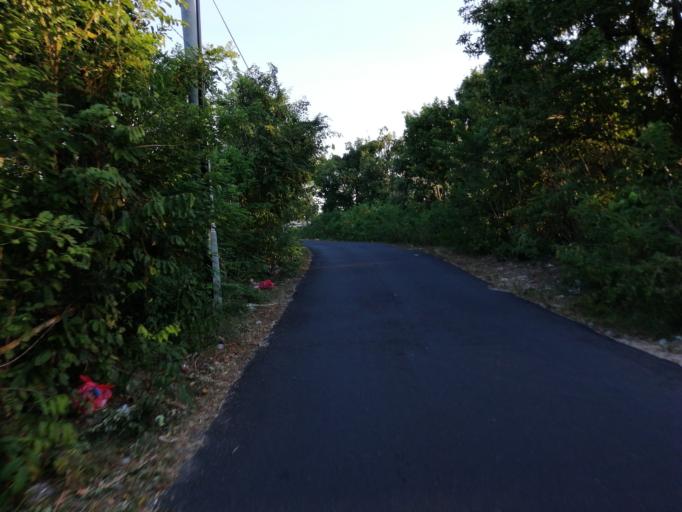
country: ID
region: Bali
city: Bualu
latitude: -8.8031
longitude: 115.1967
